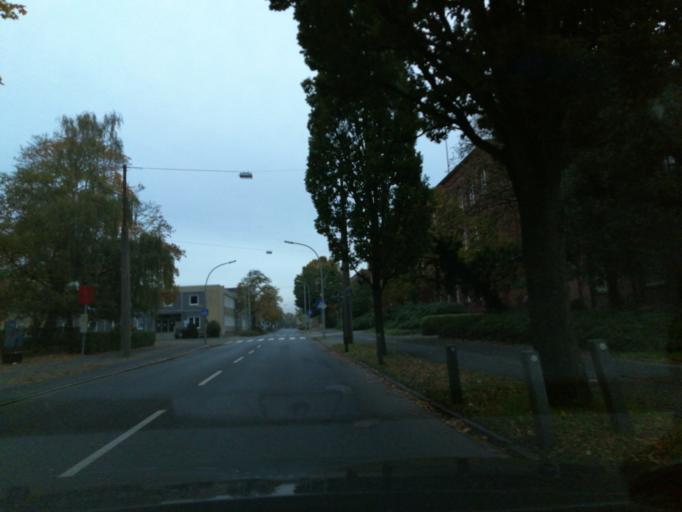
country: DE
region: Lower Saxony
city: Wilhelmshaven
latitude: 53.5189
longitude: 8.1237
